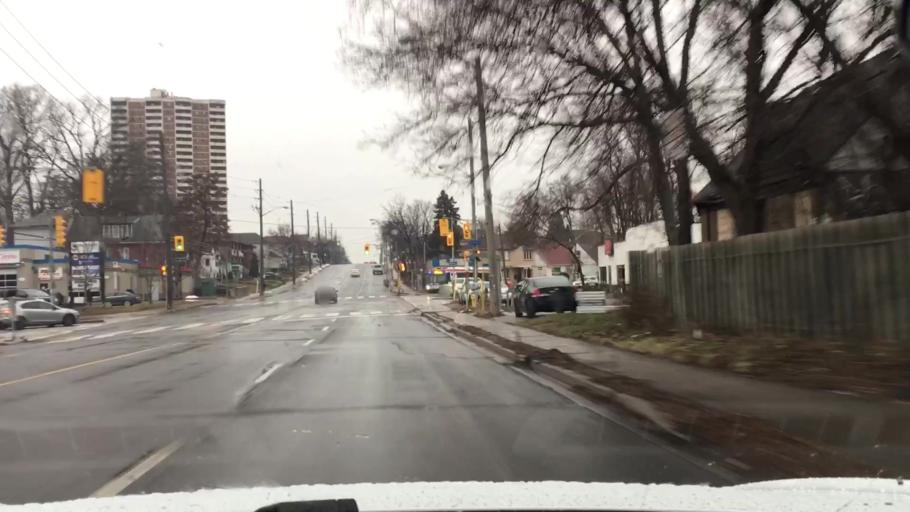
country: CA
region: Ontario
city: Scarborough
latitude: 43.6967
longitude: -79.2746
